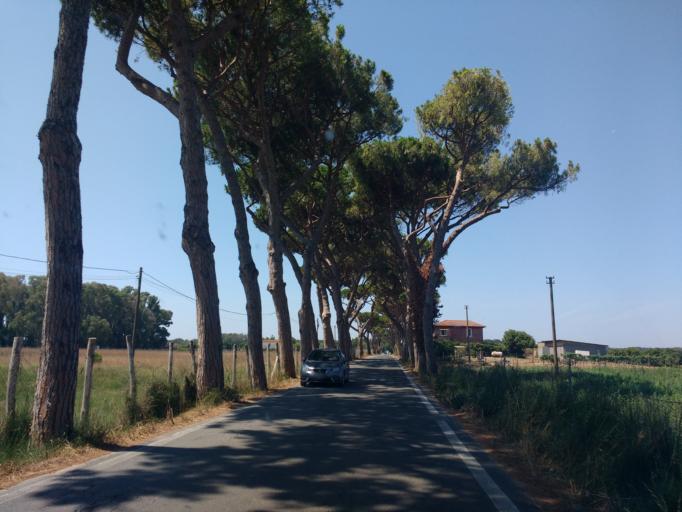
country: IT
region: Latium
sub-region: Citta metropolitana di Roma Capitale
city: Maccarese
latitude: 41.8798
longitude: 12.1916
